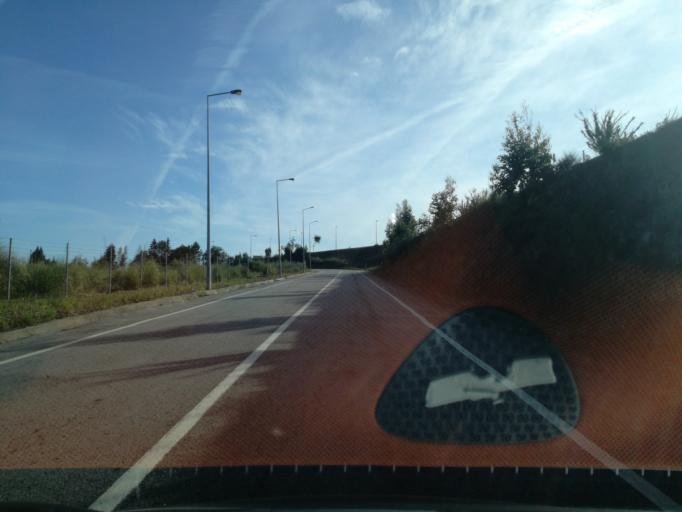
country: PT
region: Porto
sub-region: Trofa
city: Sao Romao do Coronado
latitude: 41.2847
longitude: -8.5171
